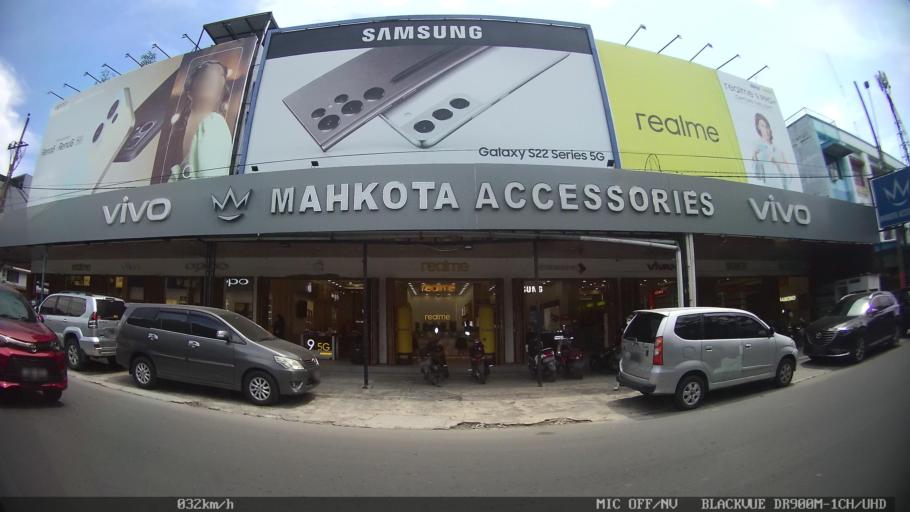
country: ID
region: North Sumatra
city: Binjai
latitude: 3.6000
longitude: 98.4864
